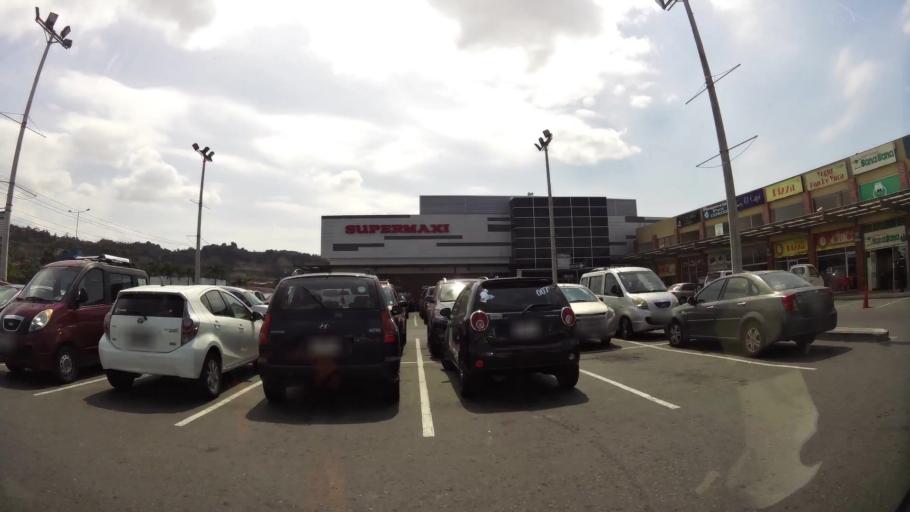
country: EC
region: Guayas
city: El Triunfo
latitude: -2.0501
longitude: -79.9141
